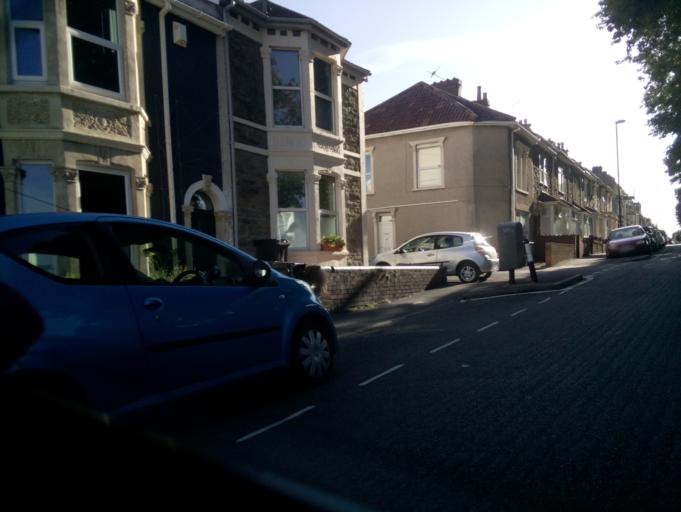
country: GB
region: England
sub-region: South Gloucestershire
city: Kingswood
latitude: 51.4578
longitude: -2.5473
